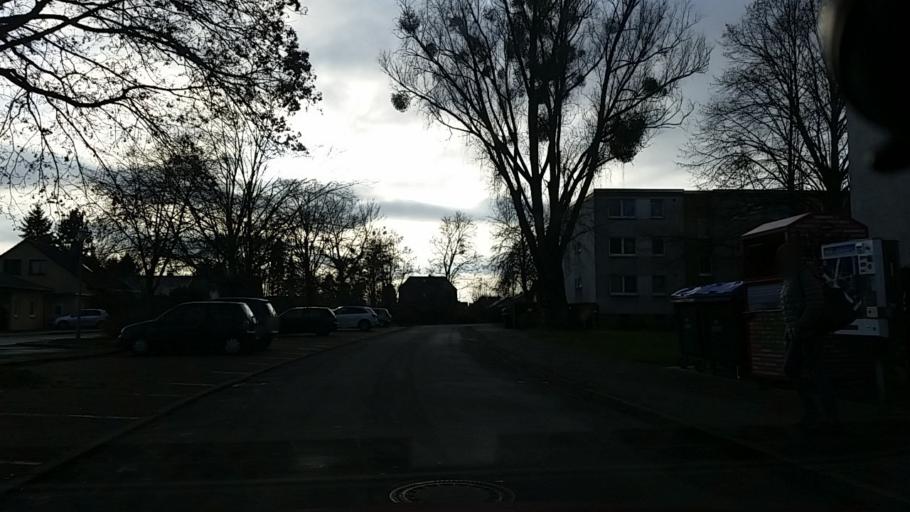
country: DE
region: Lower Saxony
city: Ruhen
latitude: 52.4510
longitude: 10.8525
